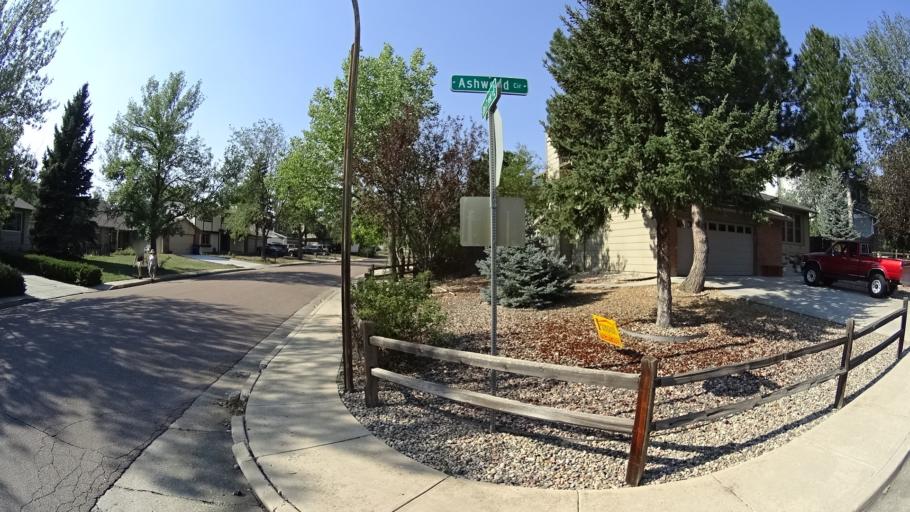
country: US
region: Colorado
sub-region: El Paso County
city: Stratmoor
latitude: 38.7835
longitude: -104.8141
